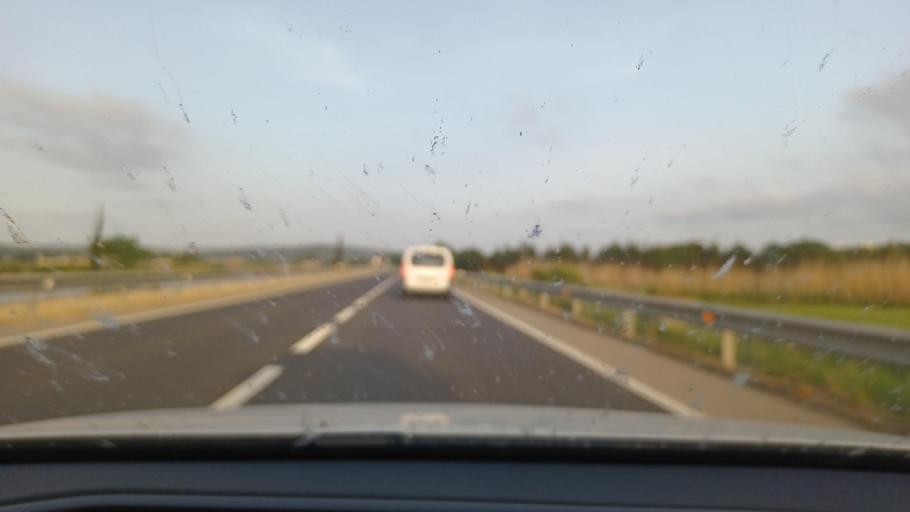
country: ES
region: Catalonia
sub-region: Provincia de Tarragona
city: Masdenverge
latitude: 40.7485
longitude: 0.5543
